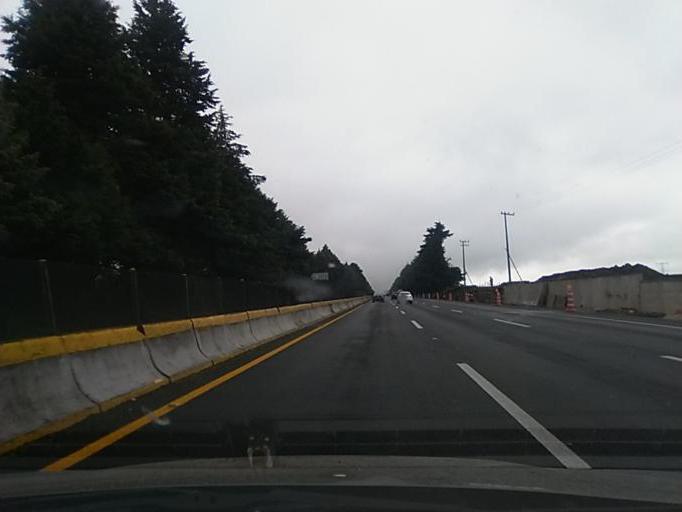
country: MX
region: Mexico City
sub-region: Tlalpan
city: Lomas de Tepemecatl
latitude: 19.1515
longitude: -99.1592
